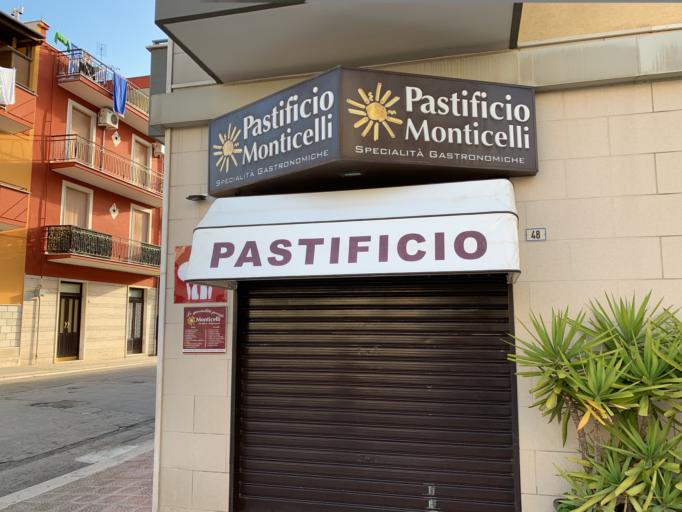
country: IT
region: Apulia
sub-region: Provincia di Barletta - Andria - Trani
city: Andria
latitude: 41.2327
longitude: 16.2879
